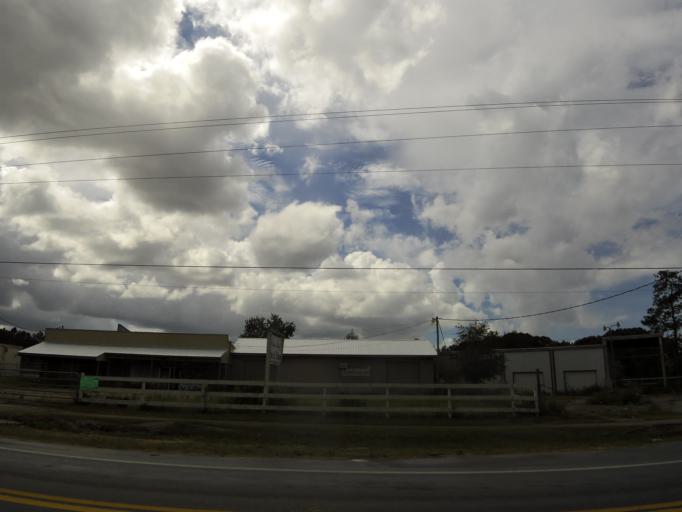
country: US
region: Florida
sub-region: Clay County
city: Middleburg
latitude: 30.0876
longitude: -81.9444
